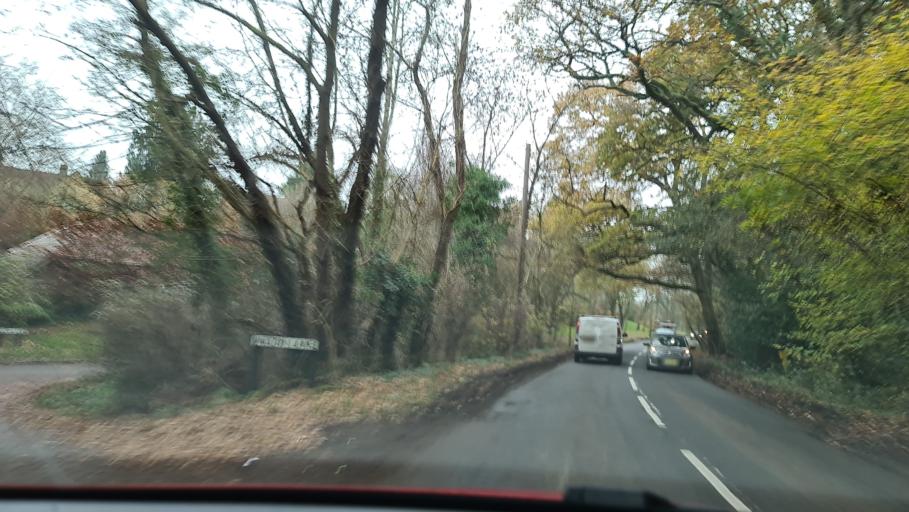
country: GB
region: England
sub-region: Buckinghamshire
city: Seer Green
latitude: 51.6176
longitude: -0.5917
